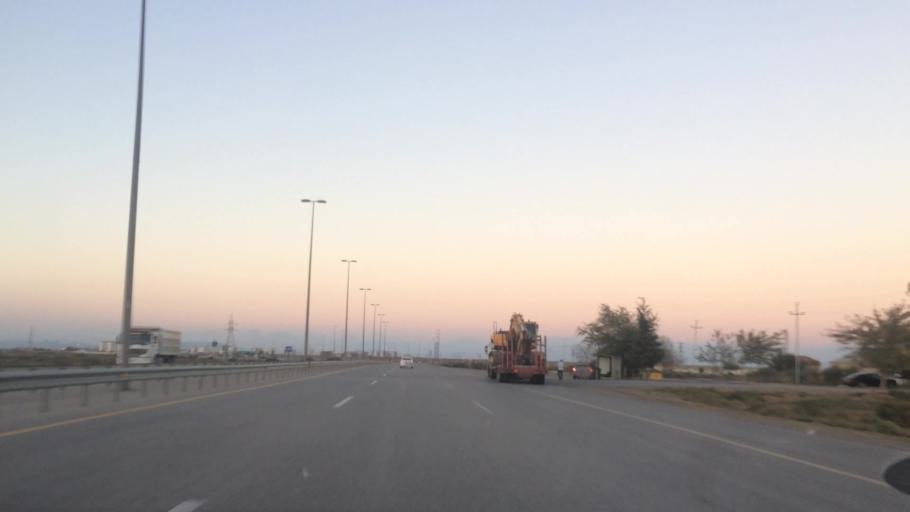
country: AZ
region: Baki
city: Qobustan
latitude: 39.9875
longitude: 49.4279
